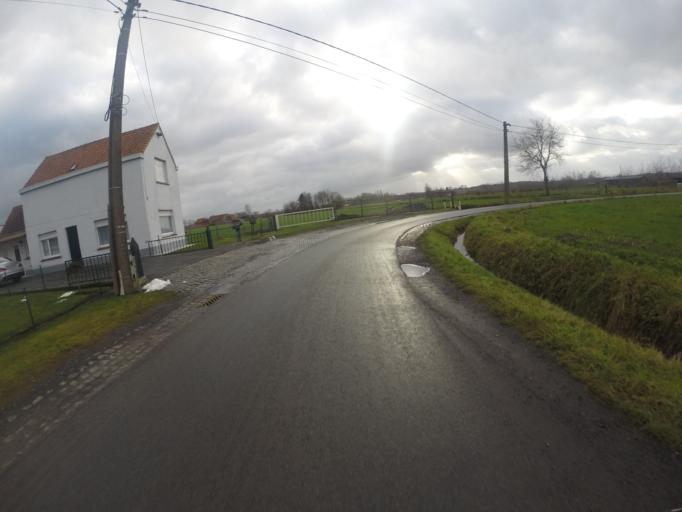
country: BE
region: Flanders
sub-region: Provincie Oost-Vlaanderen
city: Maldegem
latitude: 51.1874
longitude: 3.4652
